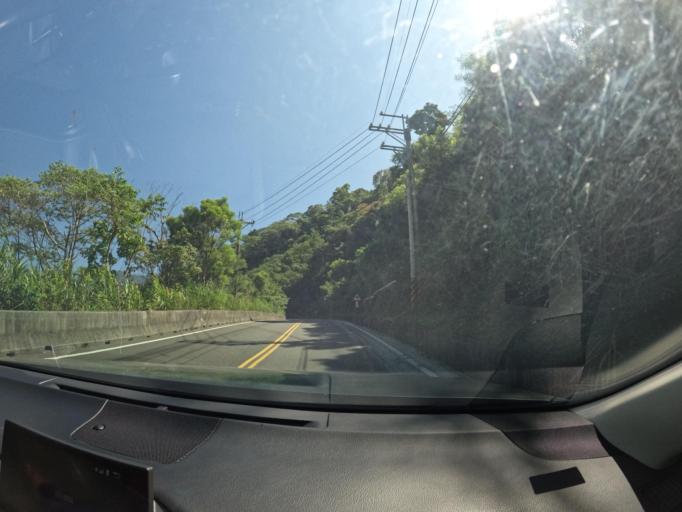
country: TW
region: Taiwan
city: Yujing
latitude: 23.1962
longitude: 120.7938
